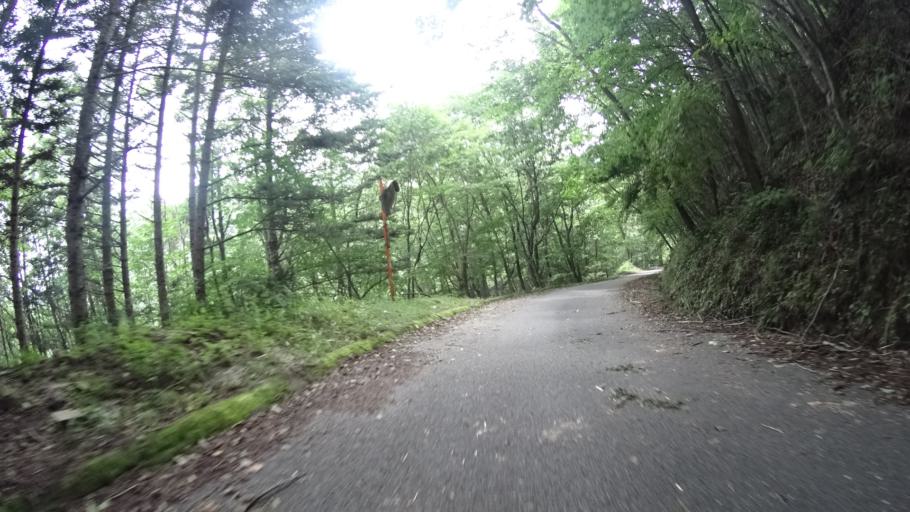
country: JP
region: Yamanashi
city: Kofu-shi
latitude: 35.8272
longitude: 138.5858
